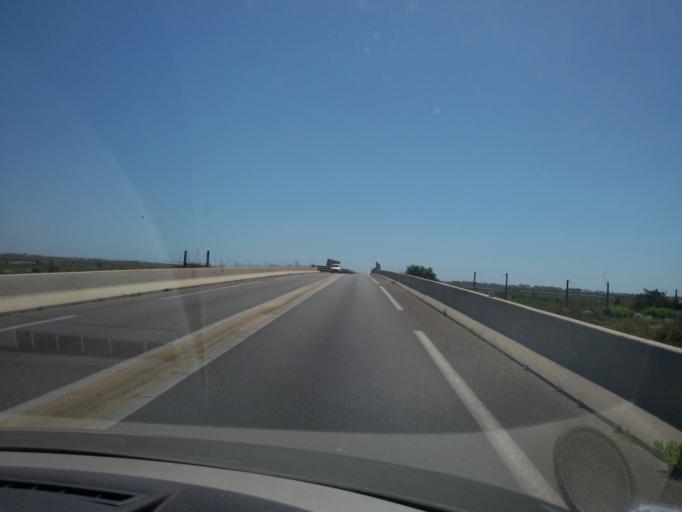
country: FR
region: Languedoc-Roussillon
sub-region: Departement de l'Herault
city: Frontignan
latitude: 43.4631
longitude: 3.7675
